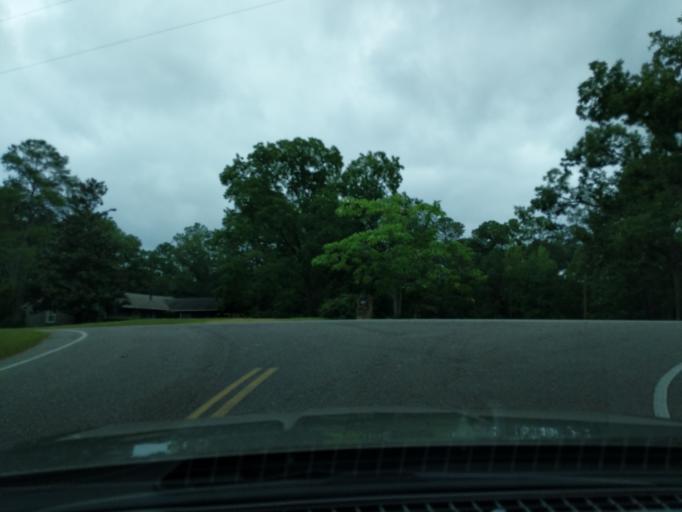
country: US
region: Georgia
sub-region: Columbia County
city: Appling
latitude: 33.6427
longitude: -82.3844
